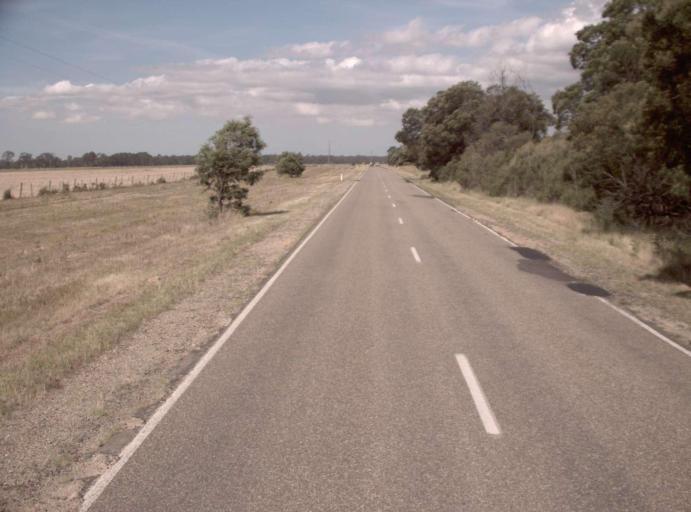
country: AU
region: Victoria
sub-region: Wellington
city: Sale
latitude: -38.1605
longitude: 146.9145
